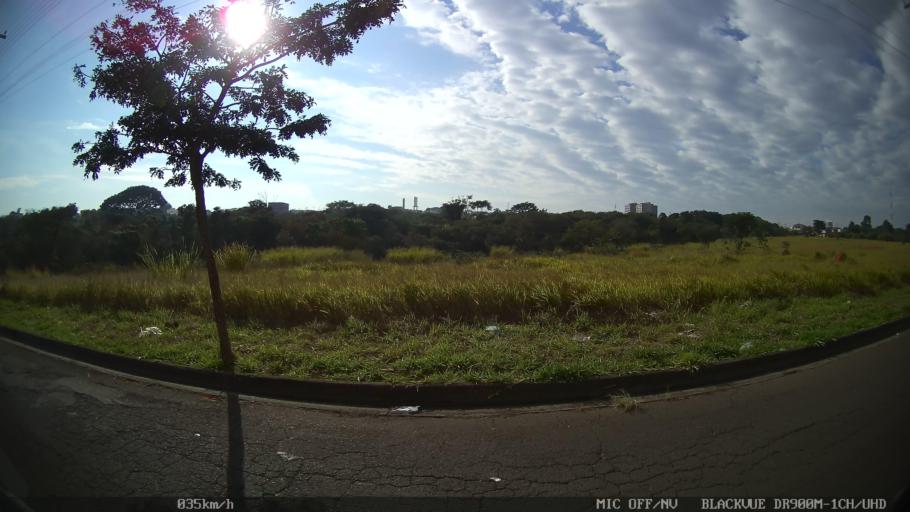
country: BR
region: Sao Paulo
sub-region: Americana
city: Americana
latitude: -22.7322
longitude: -47.3661
